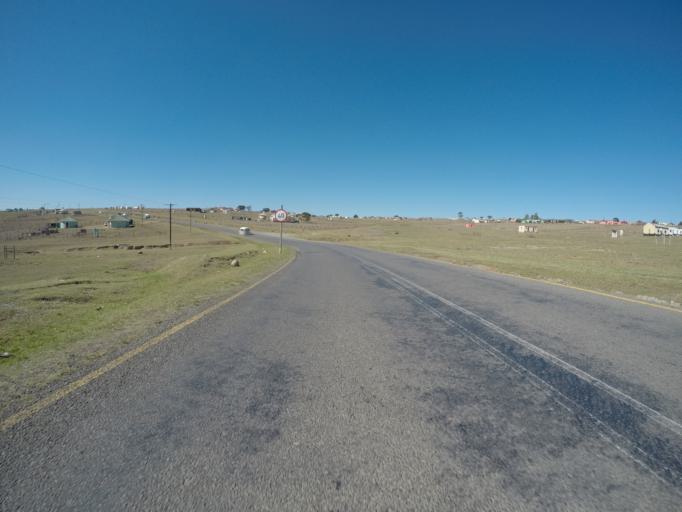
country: ZA
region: Eastern Cape
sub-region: OR Tambo District Municipality
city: Mthatha
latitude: -31.8811
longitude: 28.7557
